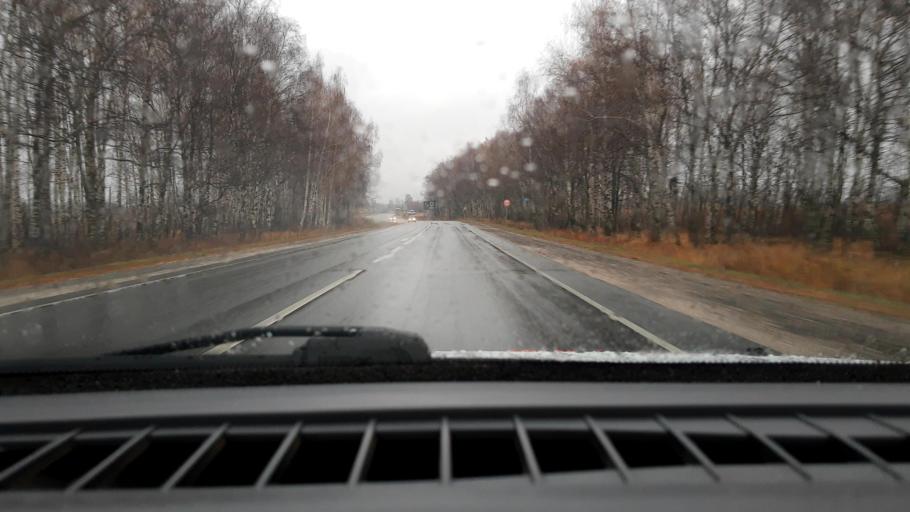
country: RU
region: Nizjnij Novgorod
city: Sitniki
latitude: 56.5389
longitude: 44.0206
